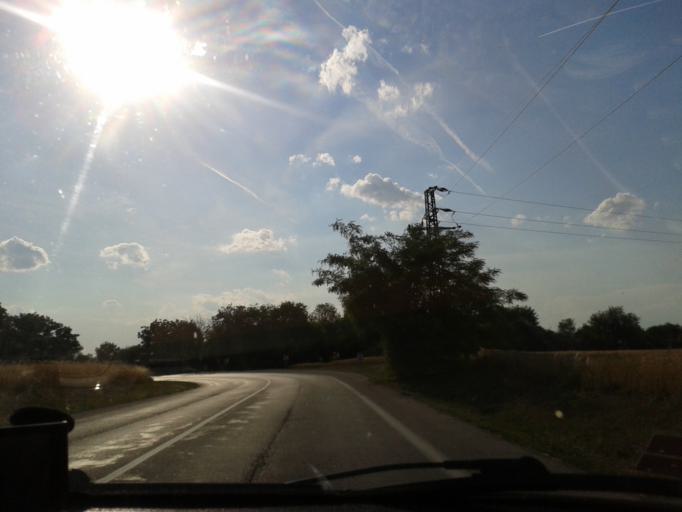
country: HU
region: Gyor-Moson-Sopron
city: Rajka
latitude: 48.0248
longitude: 17.1879
